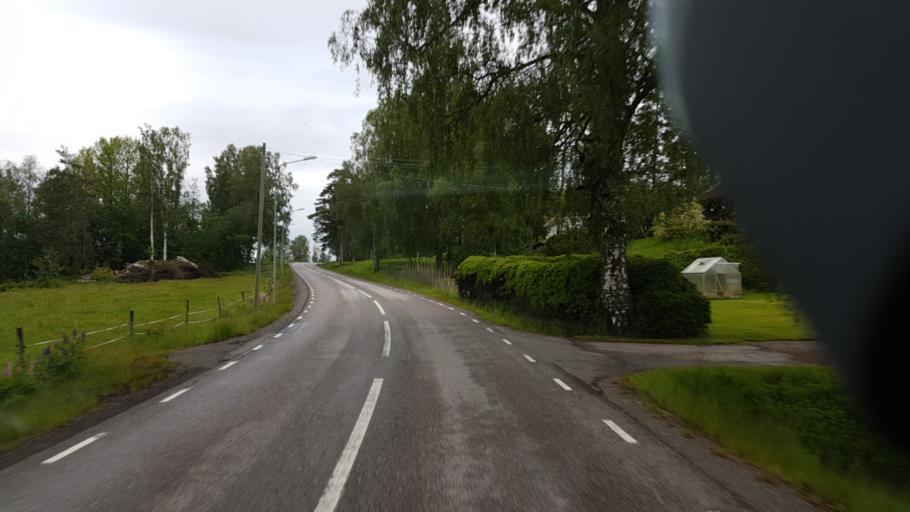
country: SE
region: Vaermland
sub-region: Eda Kommun
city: Amotfors
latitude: 59.6833
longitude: 12.1482
